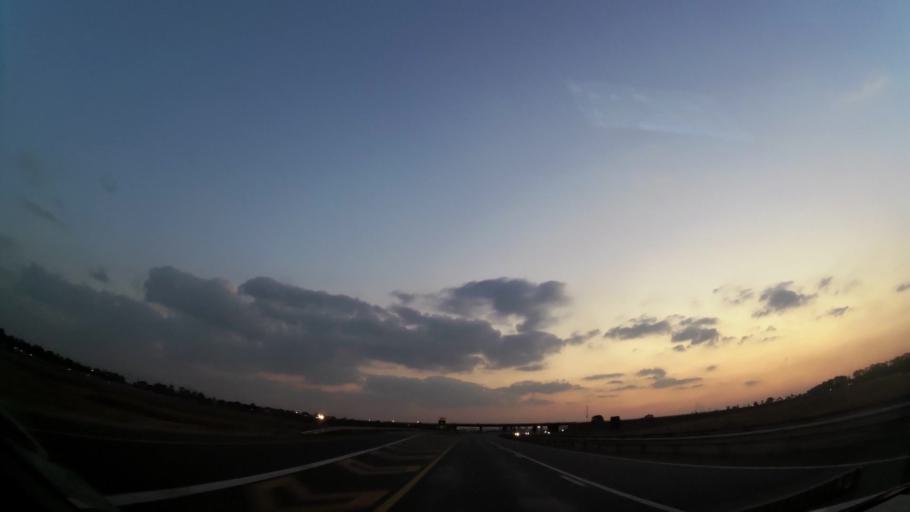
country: ZA
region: Gauteng
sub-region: Ekurhuleni Metropolitan Municipality
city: Springs
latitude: -26.2847
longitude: 28.4329
